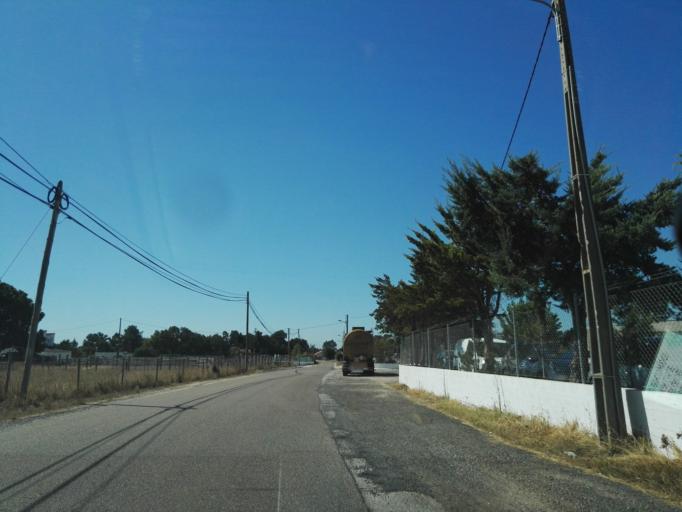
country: PT
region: Santarem
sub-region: Benavente
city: Samora Correia
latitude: 38.9118
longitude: -8.8664
